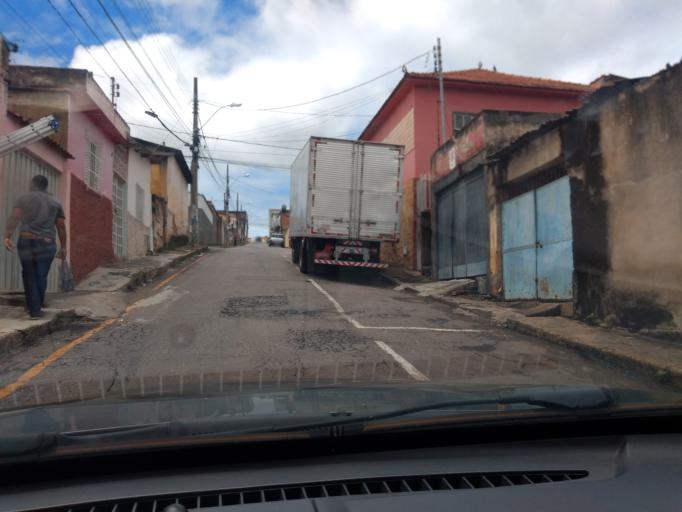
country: BR
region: Minas Gerais
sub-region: Tres Coracoes
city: Tres Coracoes
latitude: -21.6907
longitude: -45.2547
